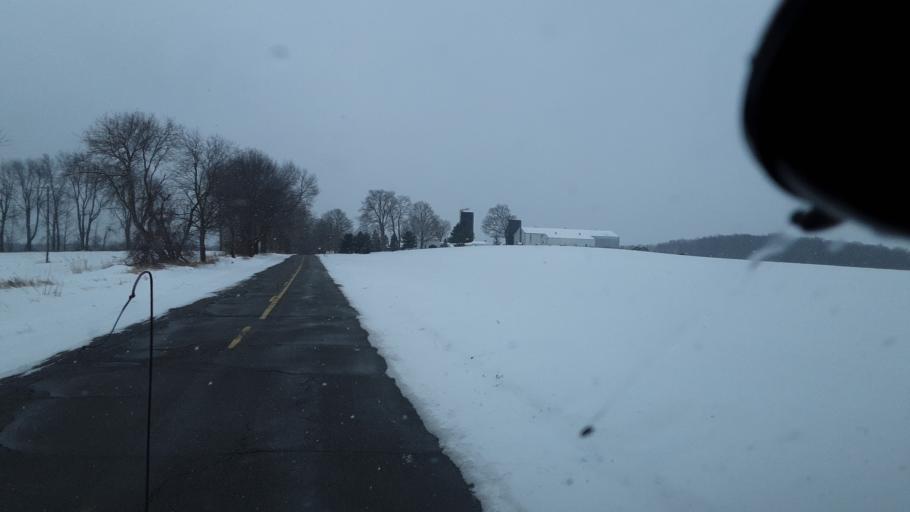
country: US
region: Michigan
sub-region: Ingham County
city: Leslie
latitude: 42.4346
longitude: -84.4775
